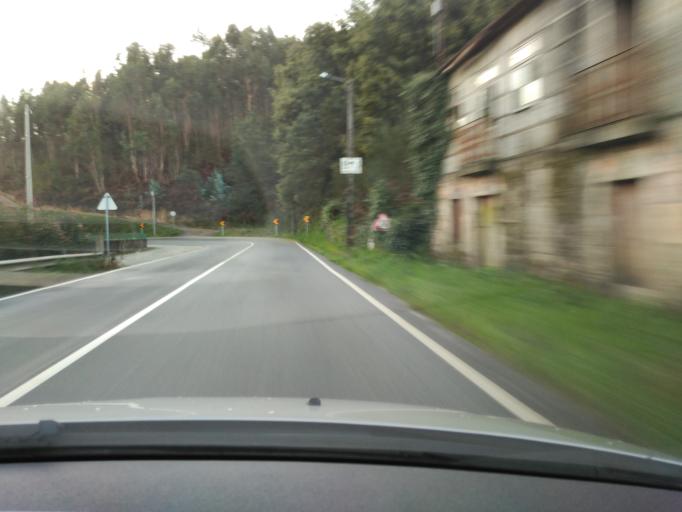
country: PT
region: Braga
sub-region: Guimaraes
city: Brito
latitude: 41.5023
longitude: -8.3884
